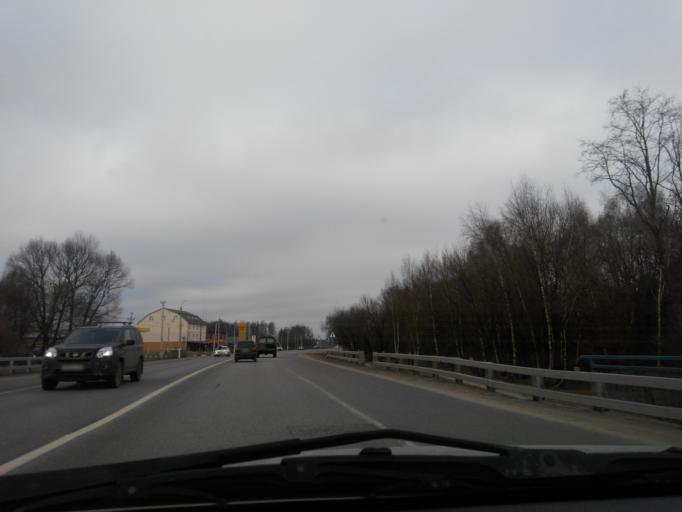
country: RU
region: Moskovskaya
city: Troitsk
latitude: 55.3416
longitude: 37.1728
